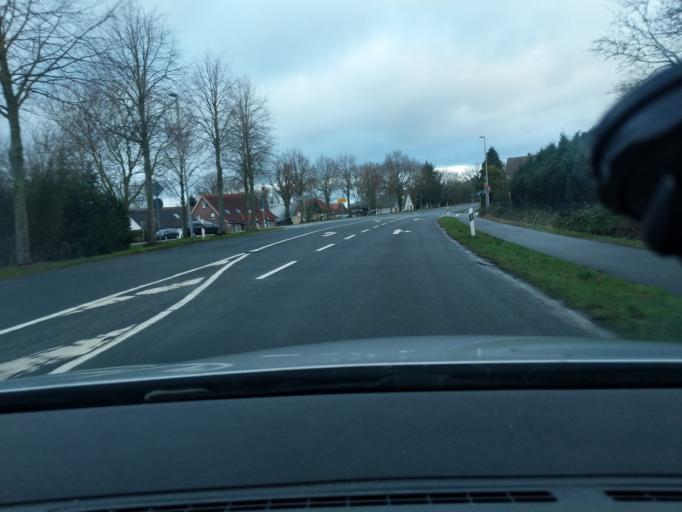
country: DE
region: Lower Saxony
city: Midlum
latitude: 53.7333
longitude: 8.6162
